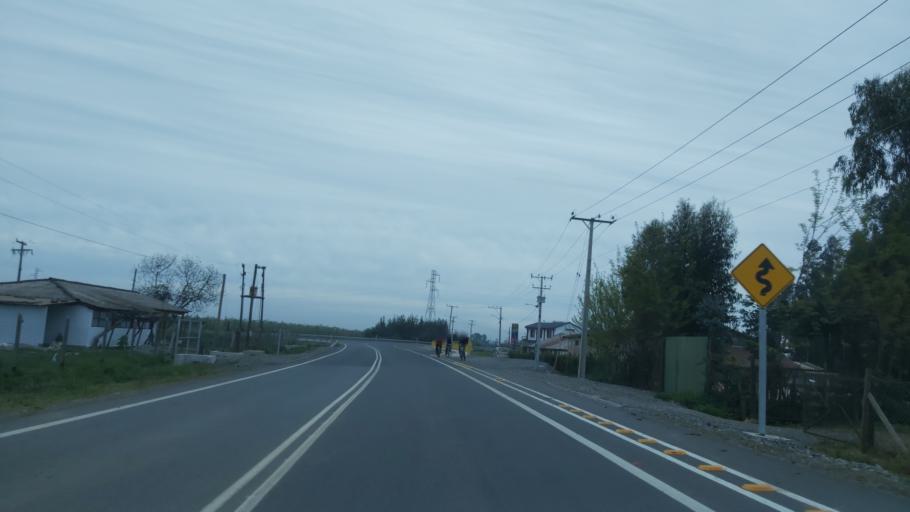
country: CL
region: Maule
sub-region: Provincia de Linares
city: Colbun
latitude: -35.6954
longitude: -71.4851
